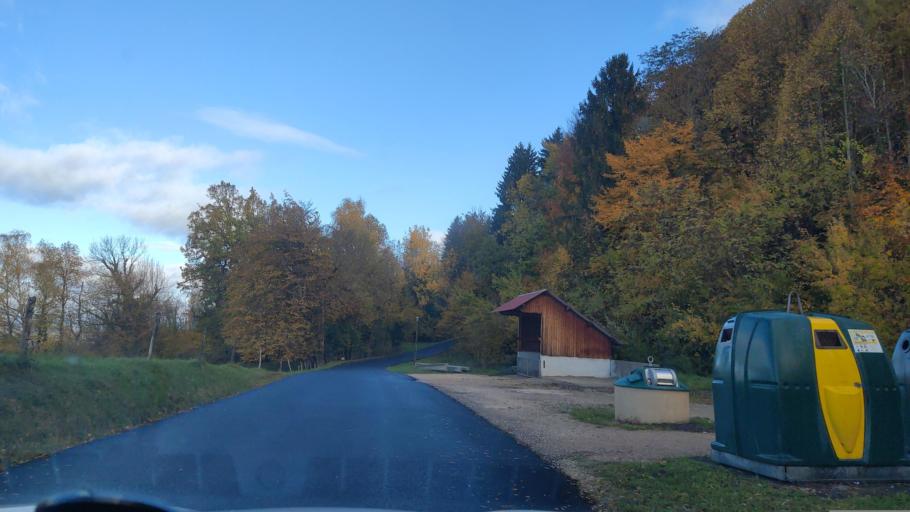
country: FR
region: Rhone-Alpes
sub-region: Departement de la Savoie
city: Novalaise
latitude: 45.6260
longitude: 5.7876
